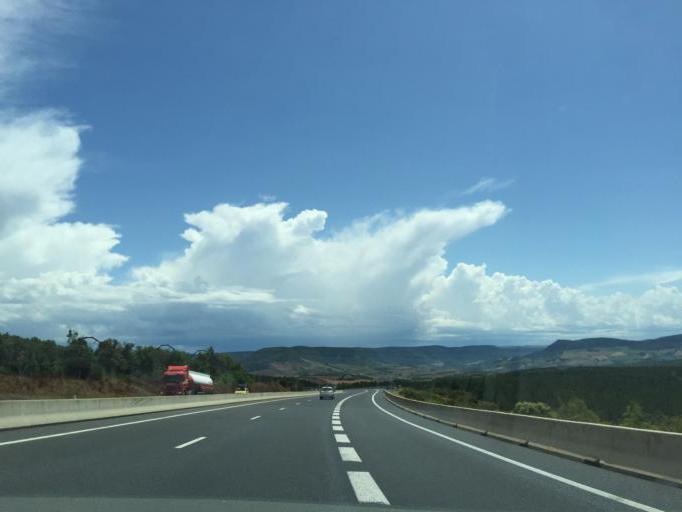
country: FR
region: Midi-Pyrenees
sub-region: Departement de l'Aveyron
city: Severac-le-Chateau
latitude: 44.2319
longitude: 3.0646
